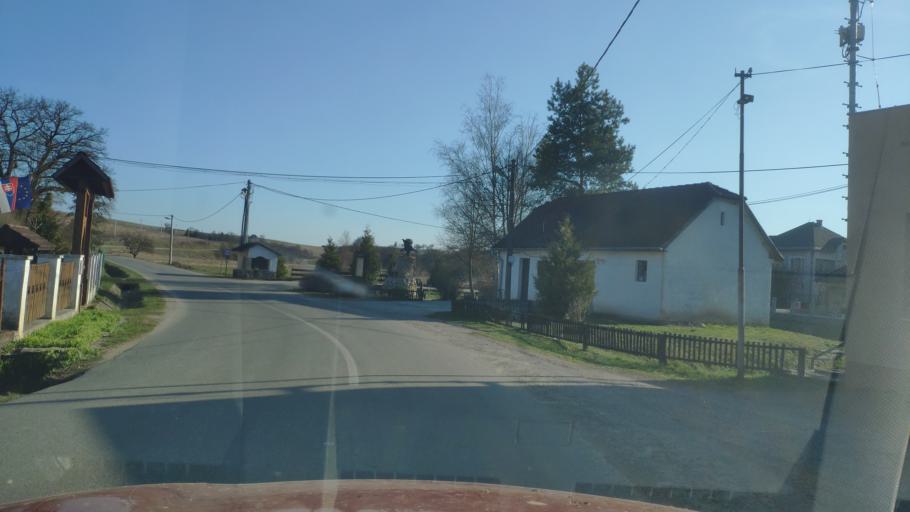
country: SK
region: Banskobystricky
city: Revuca
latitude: 48.5141
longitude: 20.2569
